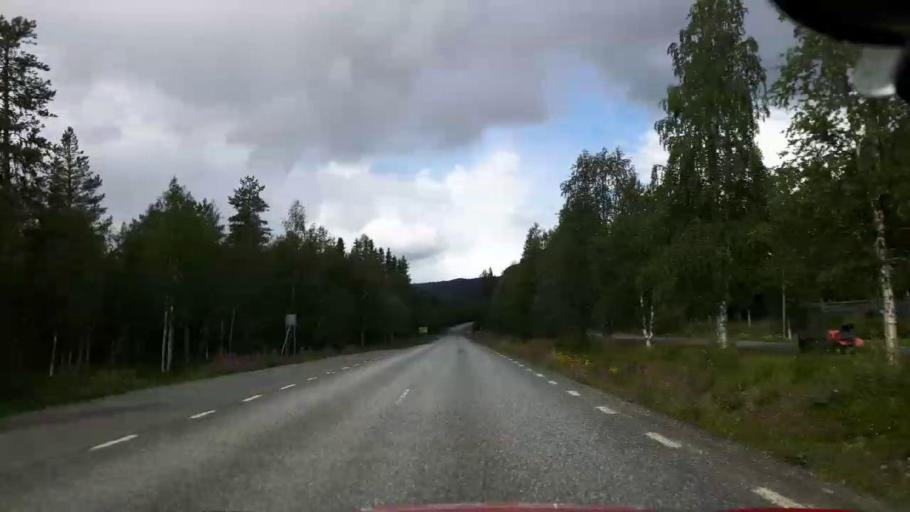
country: SE
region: Vaesterbotten
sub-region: Vilhelmina Kommun
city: Sjoberg
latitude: 64.9413
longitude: 15.8411
